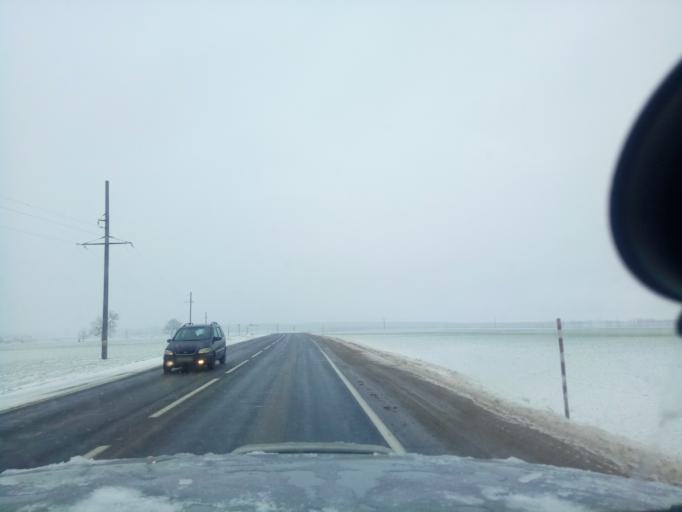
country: BY
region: Minsk
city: Nyasvizh
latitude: 53.2046
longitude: 26.6720
